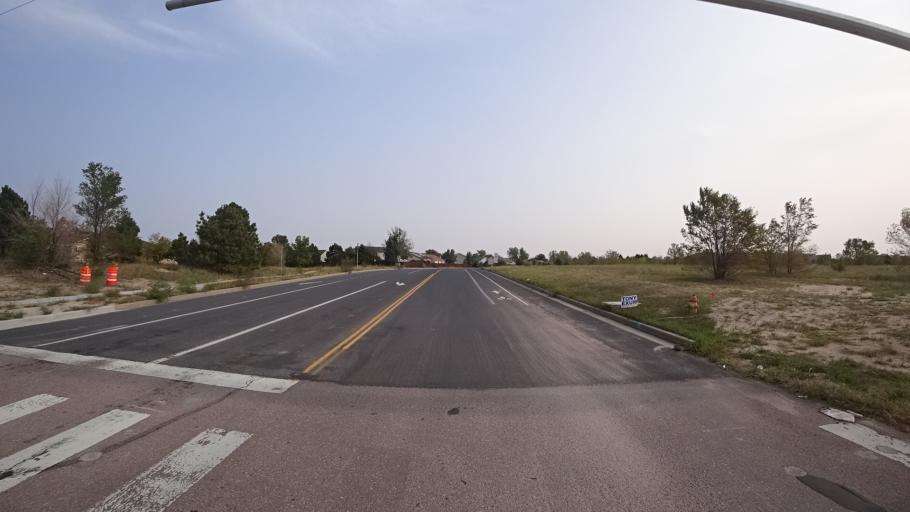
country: US
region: Colorado
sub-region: El Paso County
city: Stratmoor
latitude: 38.8070
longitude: -104.7372
